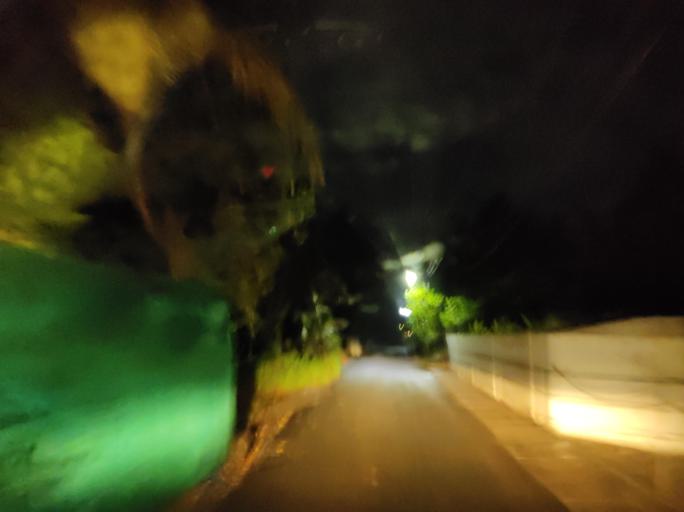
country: IN
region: Kerala
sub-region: Alappuzha
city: Arukutti
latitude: 9.8930
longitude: 76.3153
